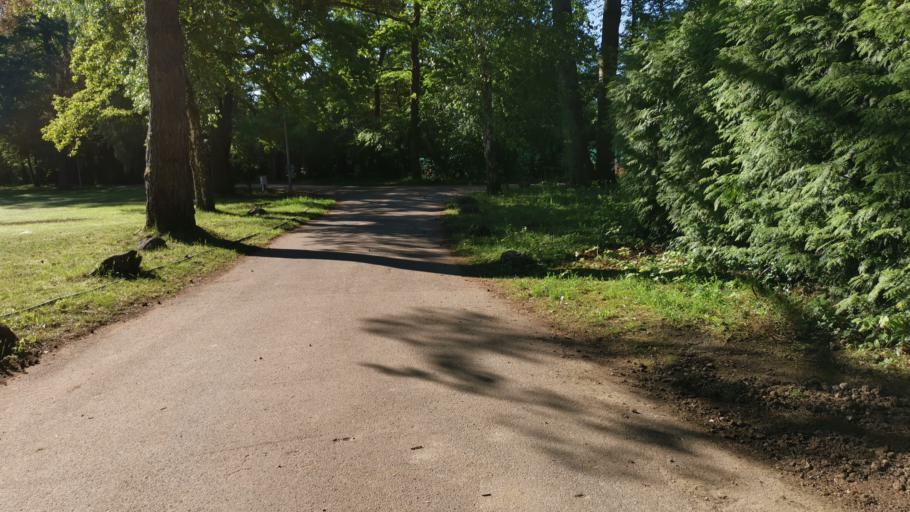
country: DE
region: Bavaria
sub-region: Upper Bavaria
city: Pullach im Isartal
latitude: 48.0892
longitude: 11.5249
